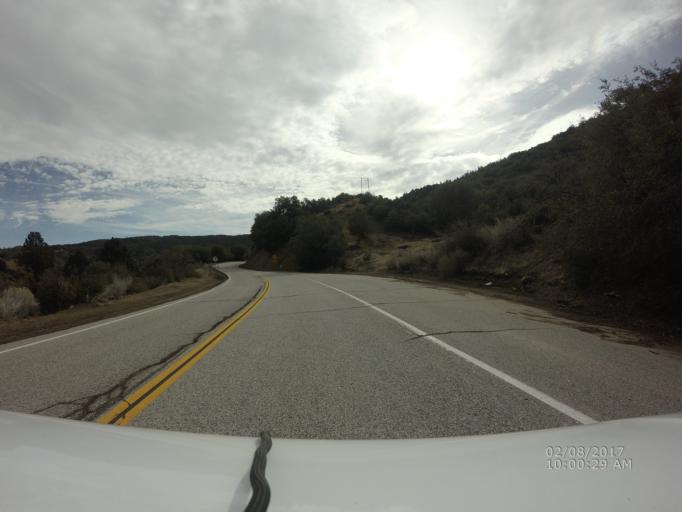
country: US
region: California
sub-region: San Bernardino County
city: Pinon Hills
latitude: 34.4046
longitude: -117.7579
